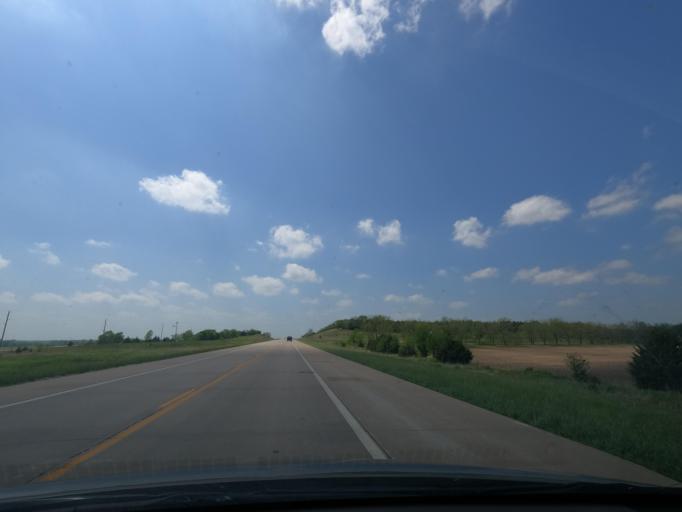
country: US
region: Kansas
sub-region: Wilson County
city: Fredonia
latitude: 37.6225
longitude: -96.0494
